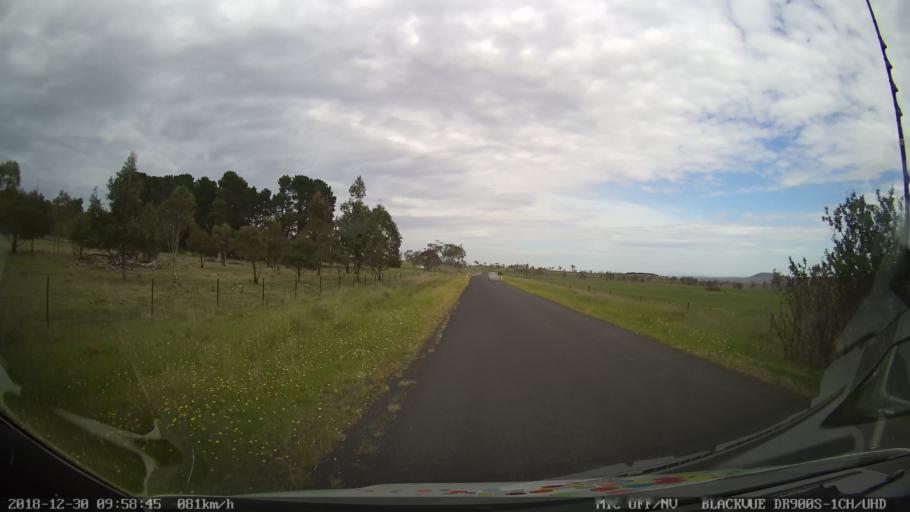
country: AU
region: New South Wales
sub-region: Cooma-Monaro
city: Cooma
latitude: -36.5223
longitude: 149.2214
